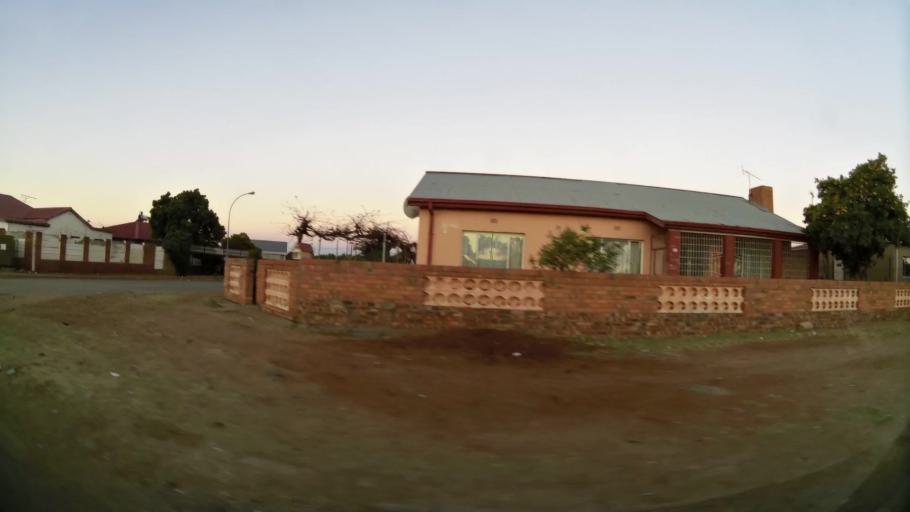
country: ZA
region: Northern Cape
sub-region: Frances Baard District Municipality
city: Kimberley
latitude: -28.7220
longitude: 24.7675
